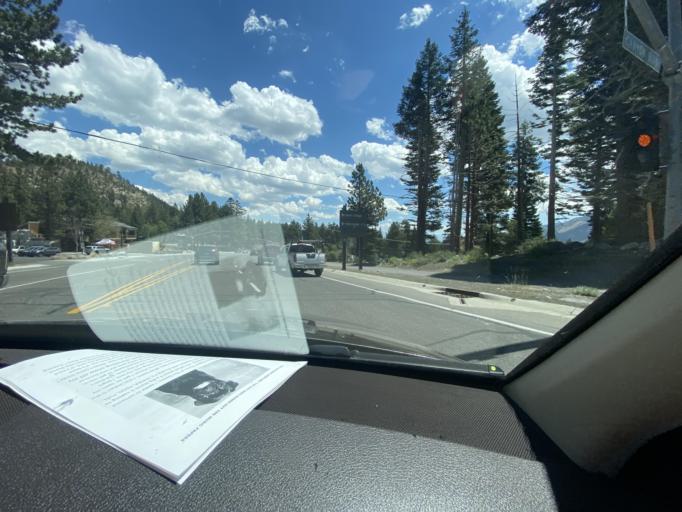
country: US
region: California
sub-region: Mono County
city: Mammoth Lakes
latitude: 37.6480
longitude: -118.9843
